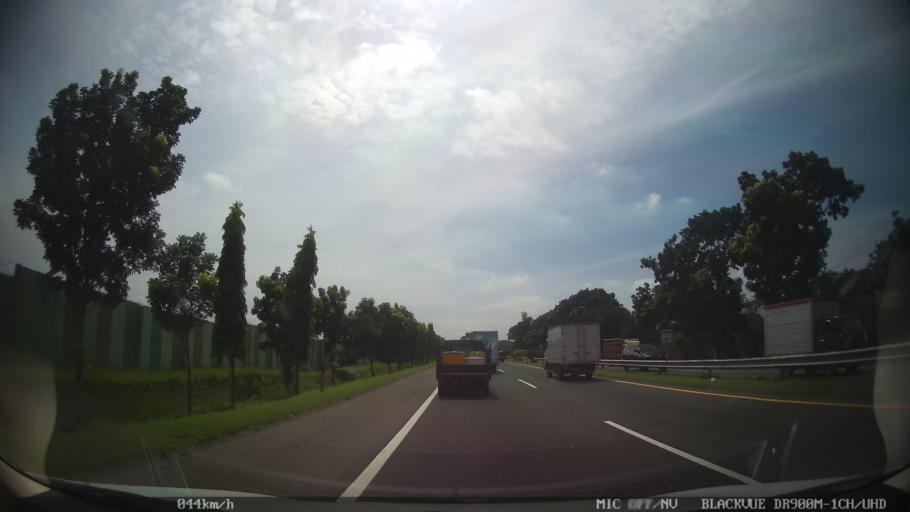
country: ID
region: North Sumatra
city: Medan
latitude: 3.6385
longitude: 98.7031
